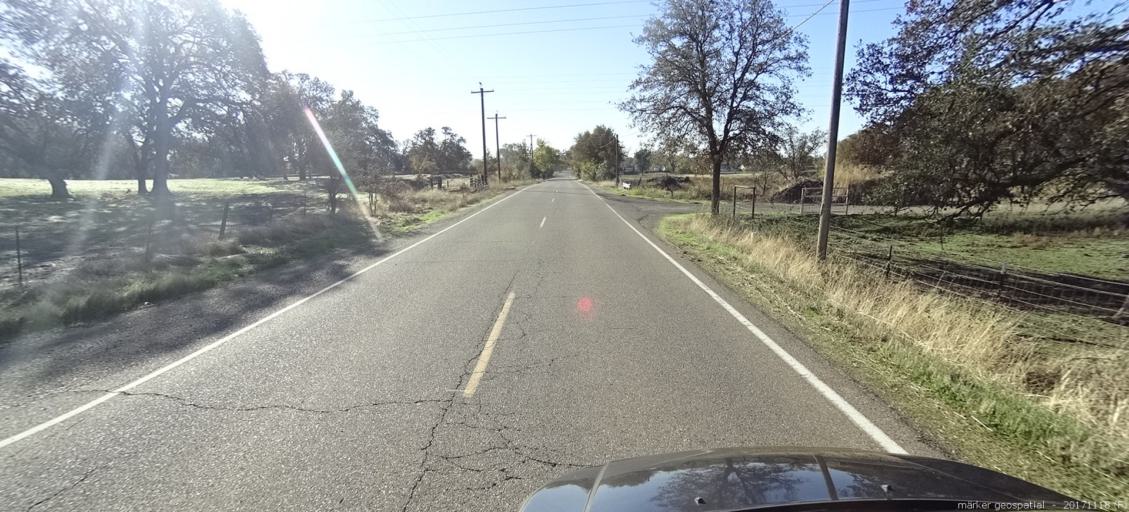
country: US
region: California
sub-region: Shasta County
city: Cottonwood
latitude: 40.4001
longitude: -122.2739
